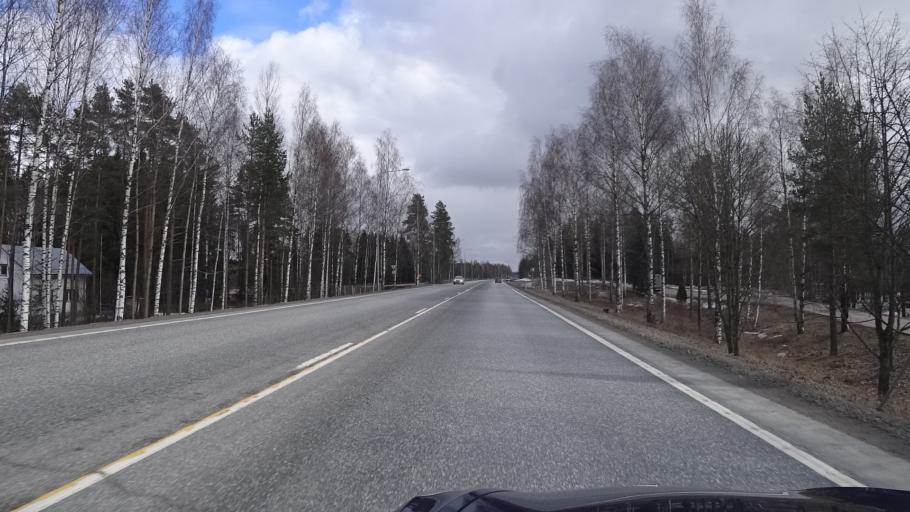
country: FI
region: Paijanne Tavastia
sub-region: Lahti
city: Nastola
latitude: 60.9515
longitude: 25.8182
